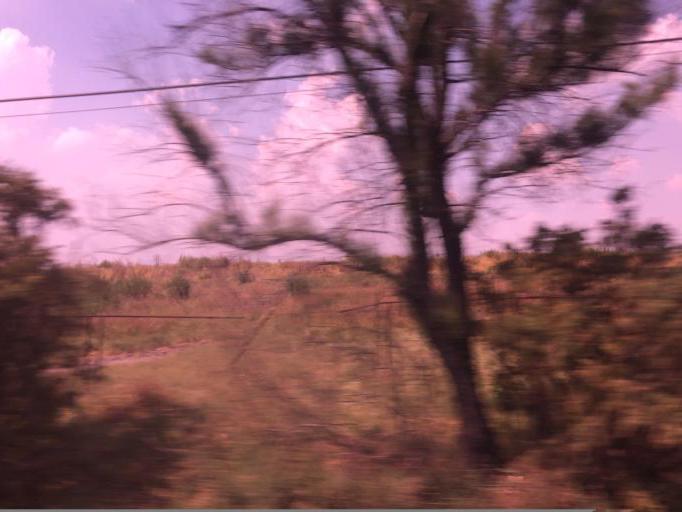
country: MX
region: Mexico
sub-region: Ciudad Nezahualcoyotl
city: Colonia Gustavo Baz Prada
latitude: 19.4602
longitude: -99.0303
